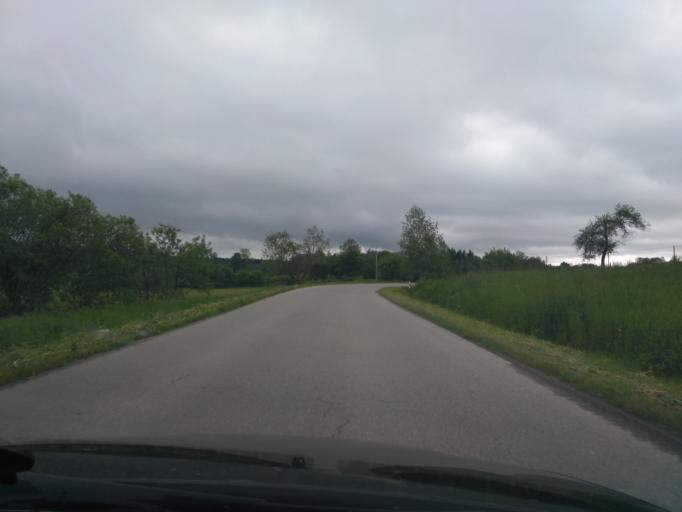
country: PL
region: Subcarpathian Voivodeship
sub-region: Powiat strzyzowski
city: Frysztak
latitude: 49.8043
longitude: 21.5471
